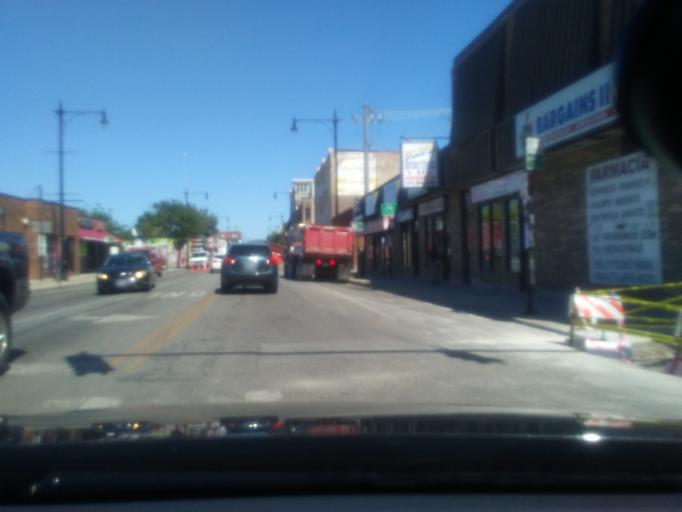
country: US
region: Illinois
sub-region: Cook County
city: Lincolnwood
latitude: 41.9684
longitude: -87.7083
